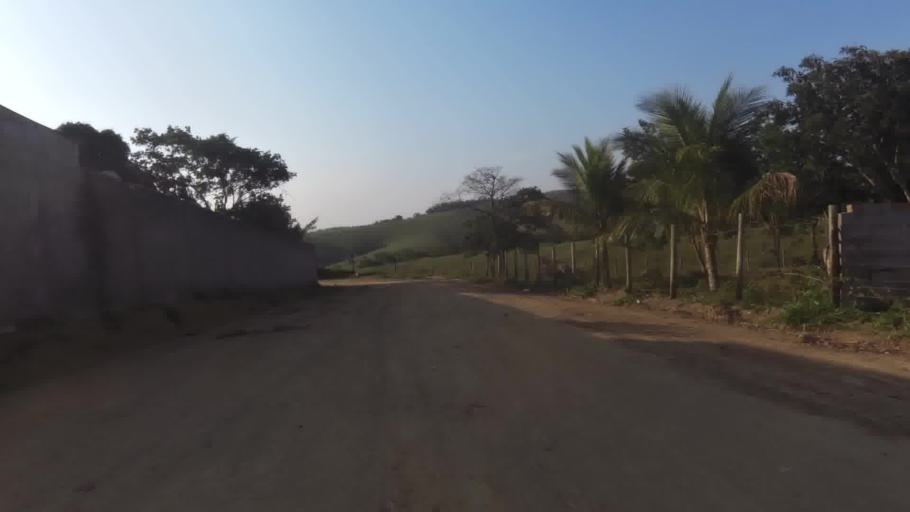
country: BR
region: Espirito Santo
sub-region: Piuma
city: Piuma
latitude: -20.8224
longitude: -40.7183
